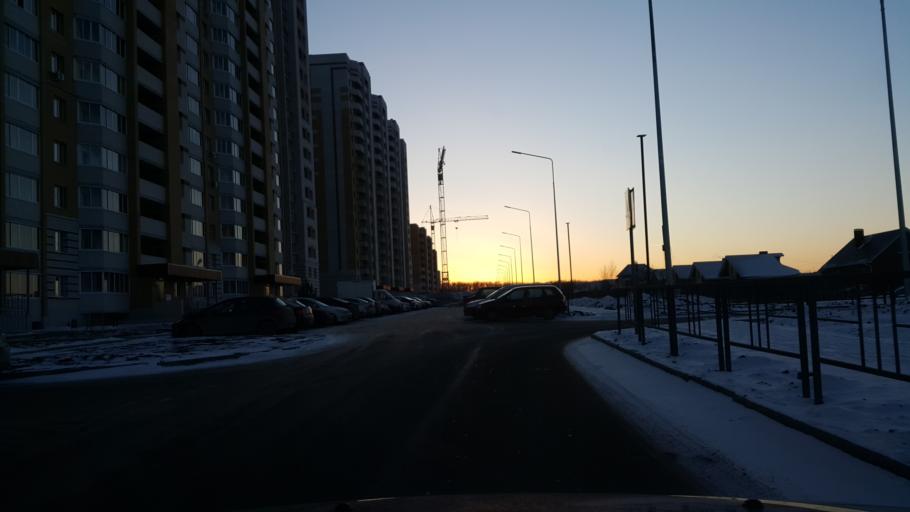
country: RU
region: Tambov
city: Tambov
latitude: 52.7598
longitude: 41.3934
